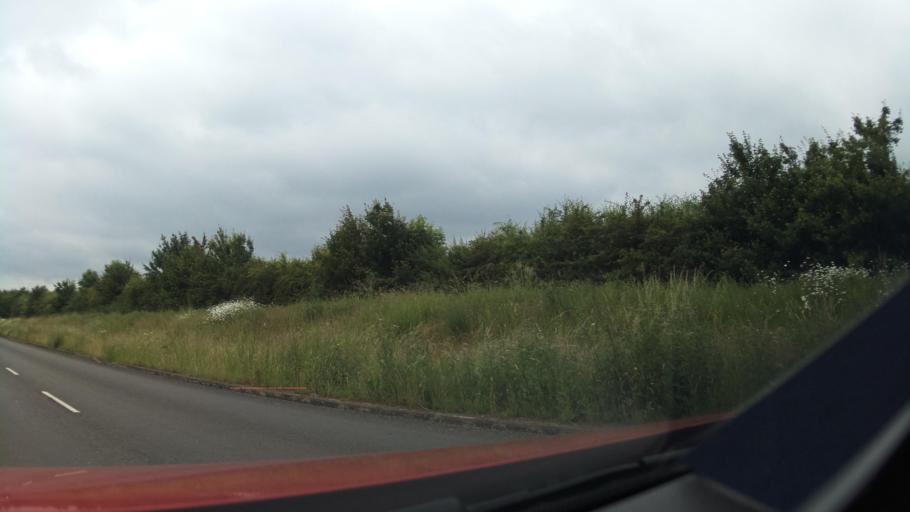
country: GB
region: England
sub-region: District of Rutland
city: Oakham
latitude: 52.6626
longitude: -0.7165
